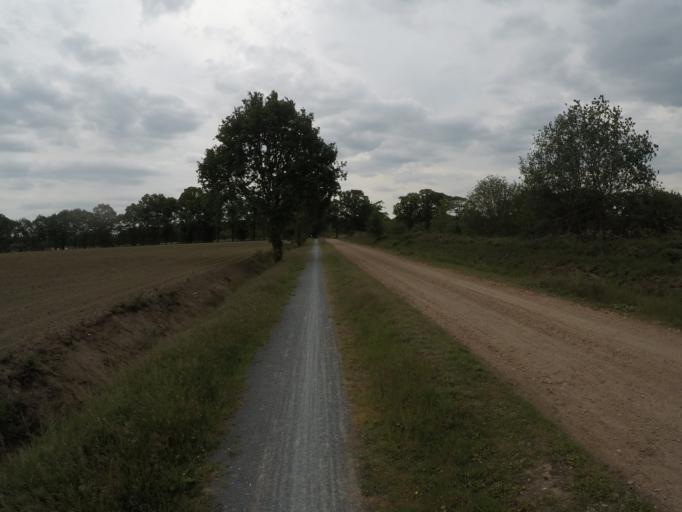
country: BE
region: Flanders
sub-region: Provincie Antwerpen
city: Oostmalle
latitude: 51.3229
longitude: 4.6954
